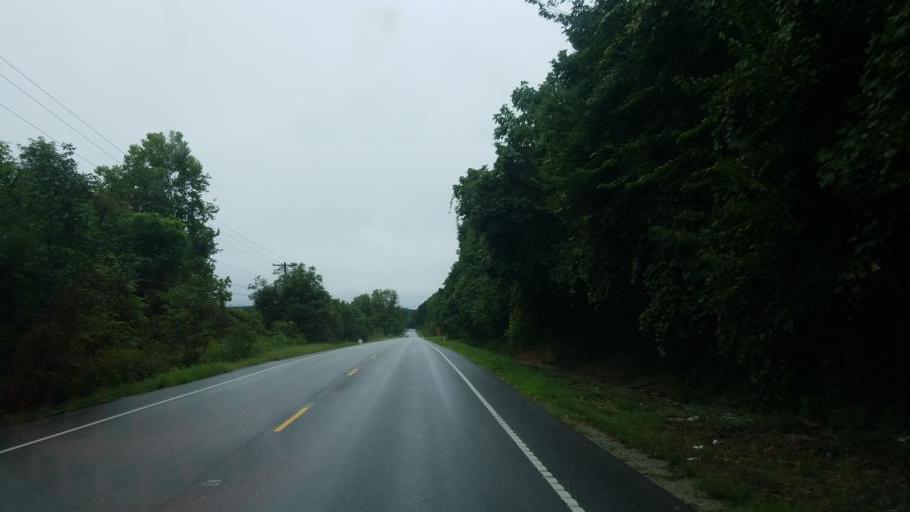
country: US
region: Ohio
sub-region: Adams County
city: Manchester
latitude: 38.6670
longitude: -83.6383
